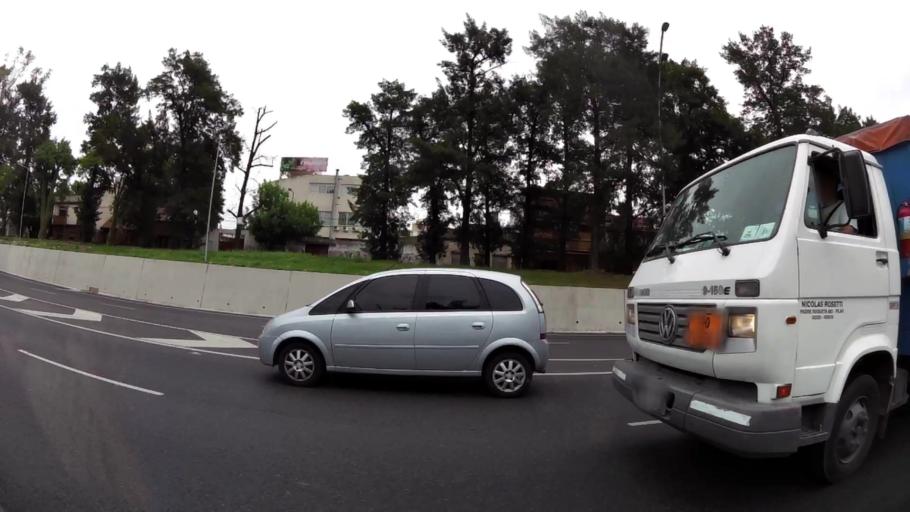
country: AR
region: Buenos Aires
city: Caseros
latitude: -34.6094
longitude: -58.5282
